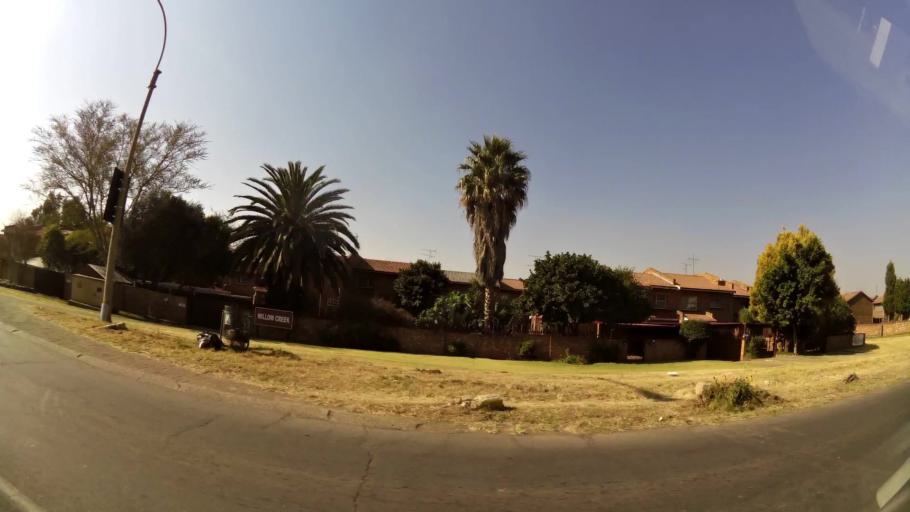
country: ZA
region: Gauteng
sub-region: City of Johannesburg Metropolitan Municipality
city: Modderfontein
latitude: -26.1162
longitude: 28.1691
